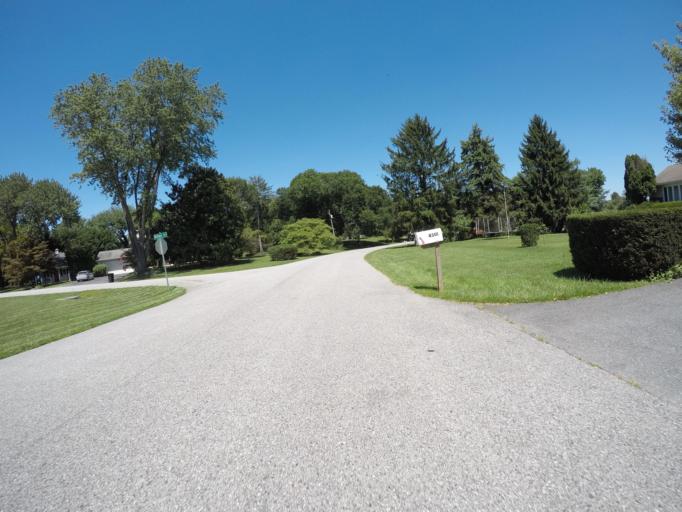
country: US
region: Maryland
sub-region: Howard County
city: Ellicott City
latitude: 39.2526
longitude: -76.8078
